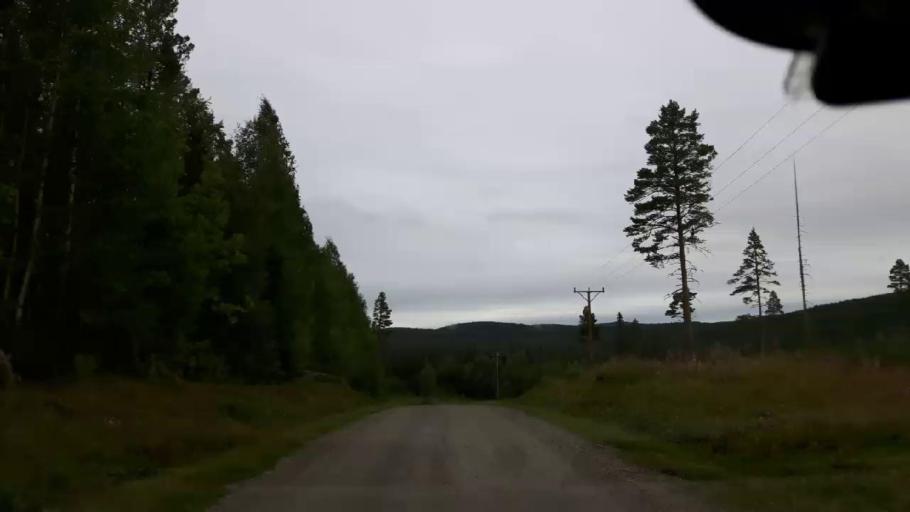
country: SE
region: Vaesternorrland
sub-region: Ange Kommun
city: Ange
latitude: 62.8550
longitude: 15.9075
